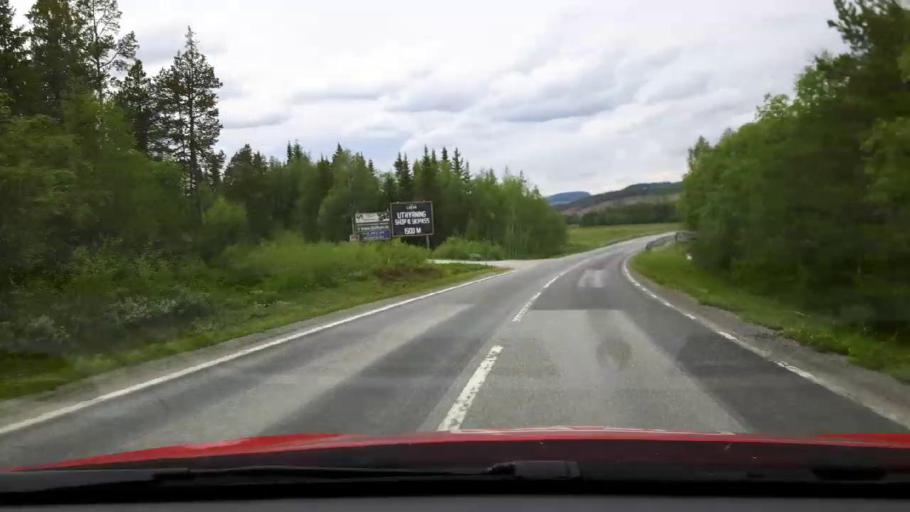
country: NO
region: Hedmark
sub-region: Engerdal
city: Engerdal
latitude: 62.4269
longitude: 12.7218
